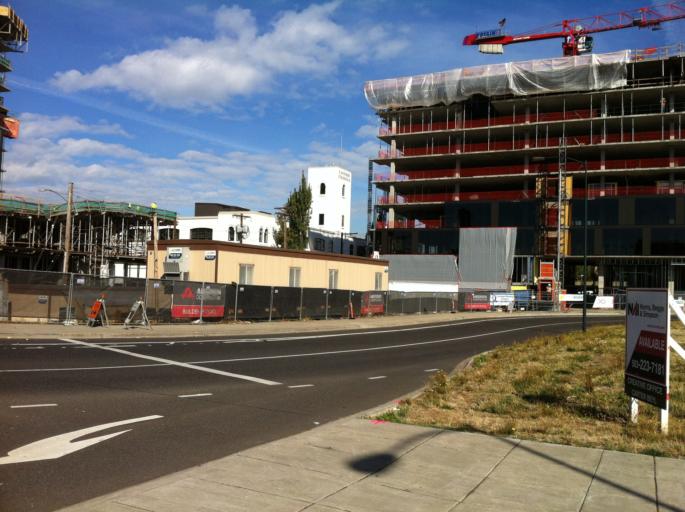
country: US
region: Oregon
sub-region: Multnomah County
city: Portland
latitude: 45.5230
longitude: -122.6622
